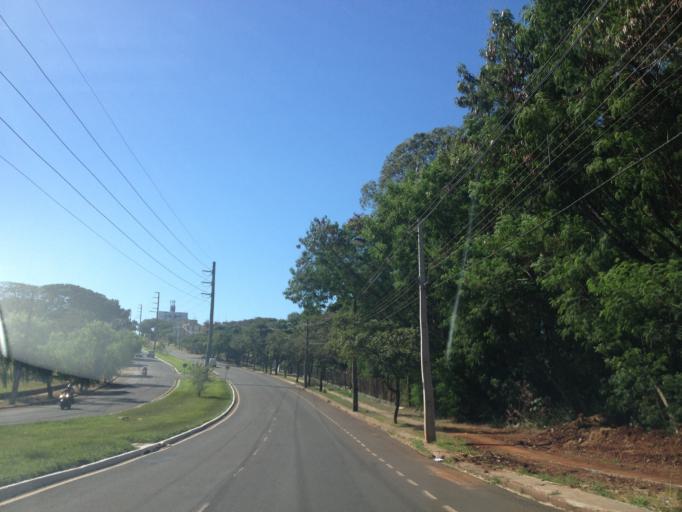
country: BR
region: Parana
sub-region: Maringa
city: Maringa
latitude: -23.4480
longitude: -51.9388
